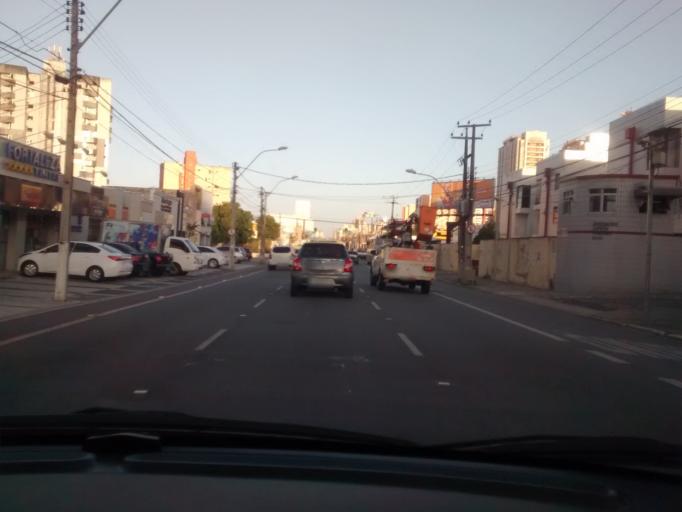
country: BR
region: Ceara
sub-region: Fortaleza
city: Fortaleza
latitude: -3.7388
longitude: -38.4904
